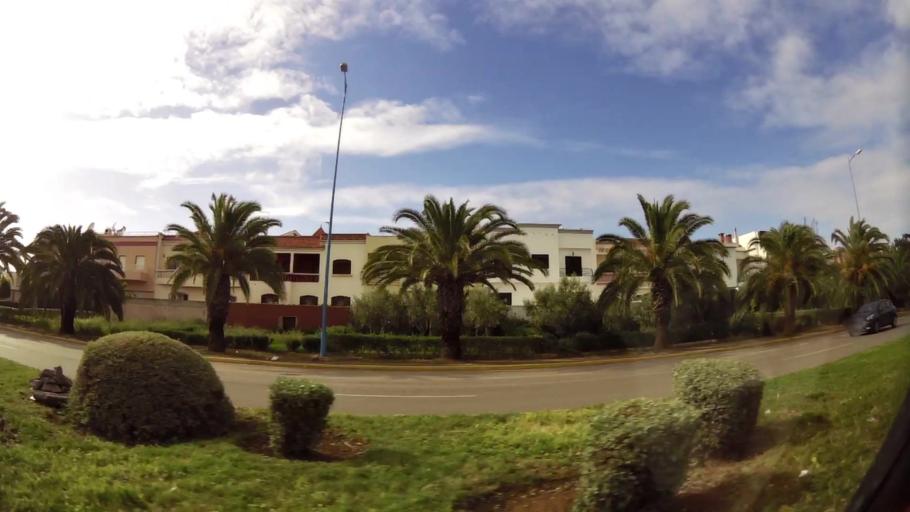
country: MA
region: Grand Casablanca
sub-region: Mohammedia
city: Mohammedia
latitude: 33.7108
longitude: -7.3464
